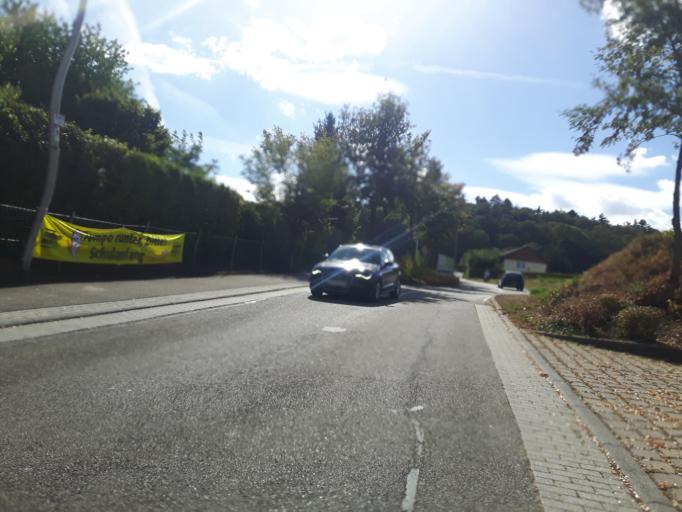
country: DE
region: Baden-Wuerttemberg
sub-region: Regierungsbezirk Stuttgart
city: Flein
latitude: 49.0980
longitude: 9.2096
